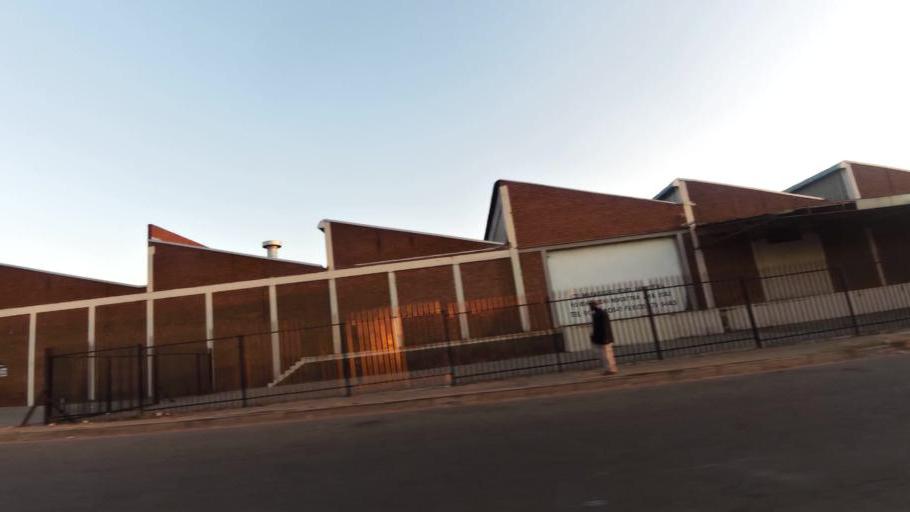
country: ZA
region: Gauteng
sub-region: City of Johannesburg Metropolitan Municipality
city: Johannesburg
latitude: -26.1974
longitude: 27.9665
